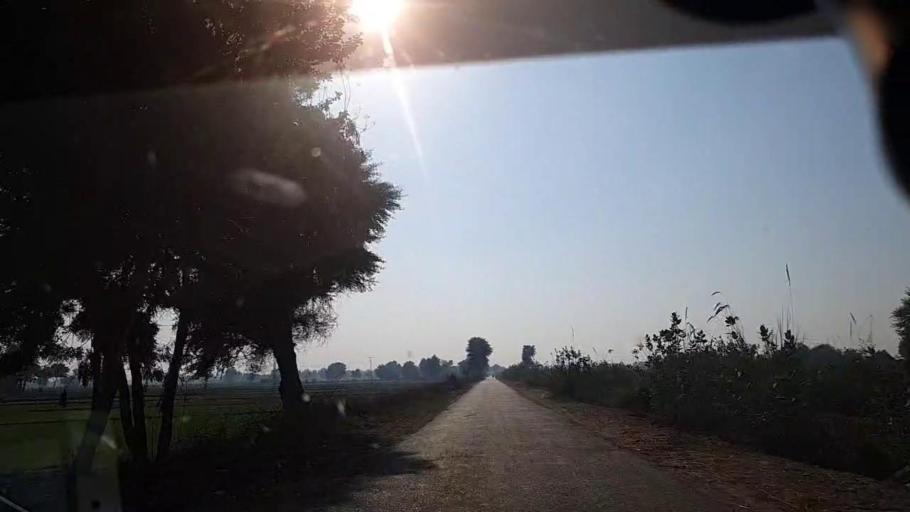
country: PK
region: Sindh
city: Sobhadero
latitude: 27.2438
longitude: 68.2882
